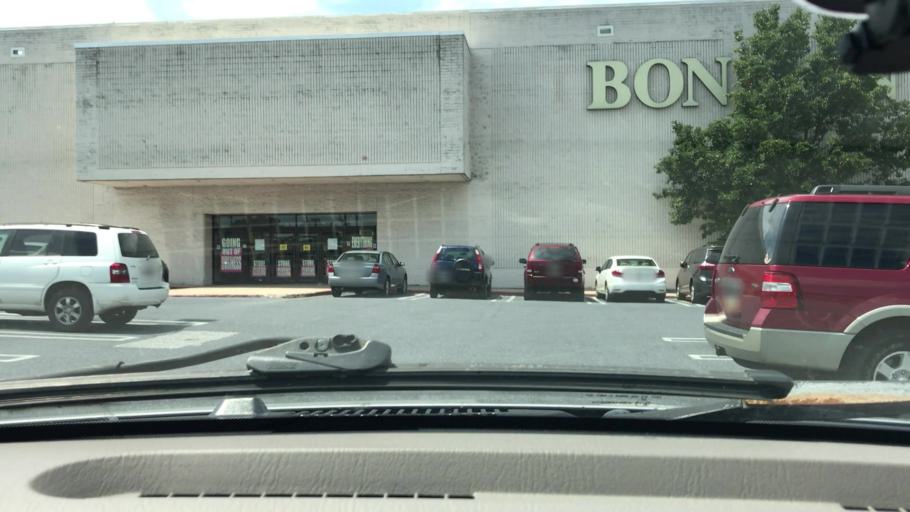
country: US
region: Pennsylvania
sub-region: Dauphin County
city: Colonial Park
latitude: 40.3013
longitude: -76.8176
